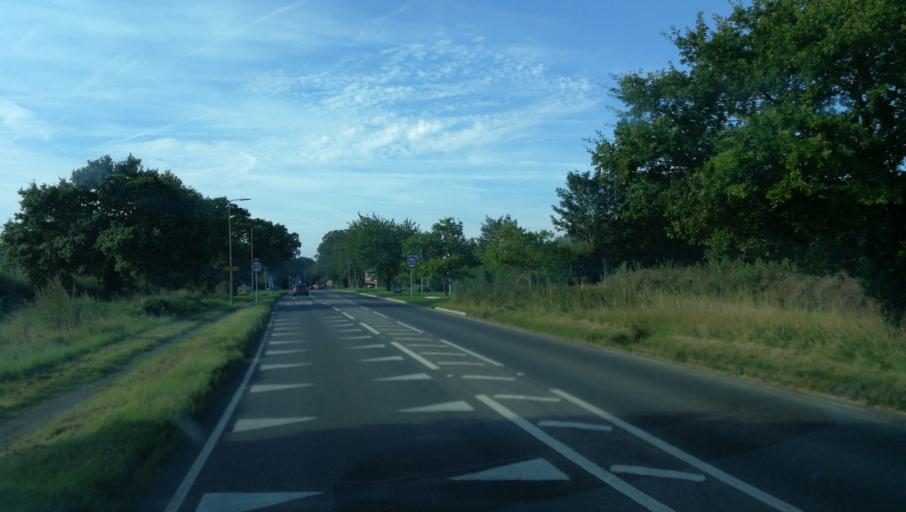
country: GB
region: England
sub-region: Oxfordshire
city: Deddington
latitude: 51.9857
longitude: -1.3224
